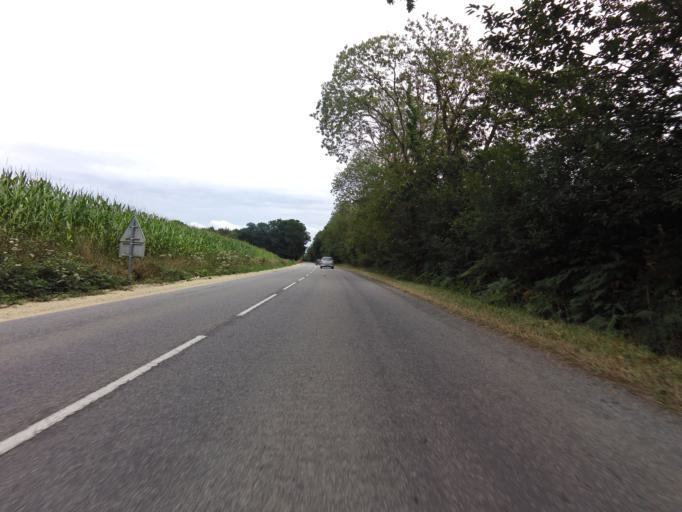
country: FR
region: Brittany
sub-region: Departement du Finistere
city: Douarnenez
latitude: 48.0811
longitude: -4.3637
